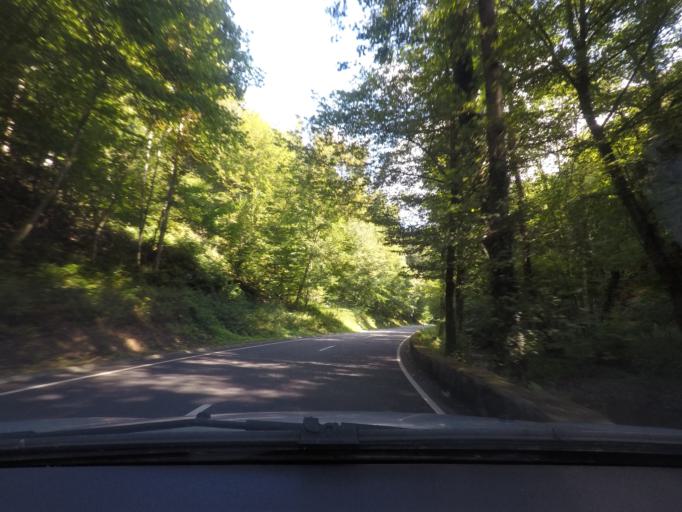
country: LU
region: Grevenmacher
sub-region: Canton d'Echternach
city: Waldbillig
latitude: 49.7647
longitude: 6.2808
